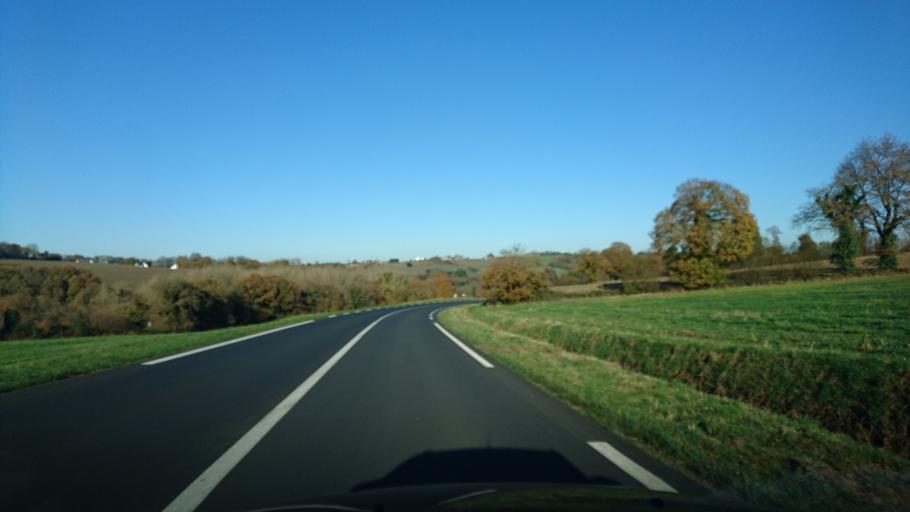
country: FR
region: Brittany
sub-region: Departement des Cotes-d'Armor
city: Pledran
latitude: 48.4616
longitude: -2.7558
